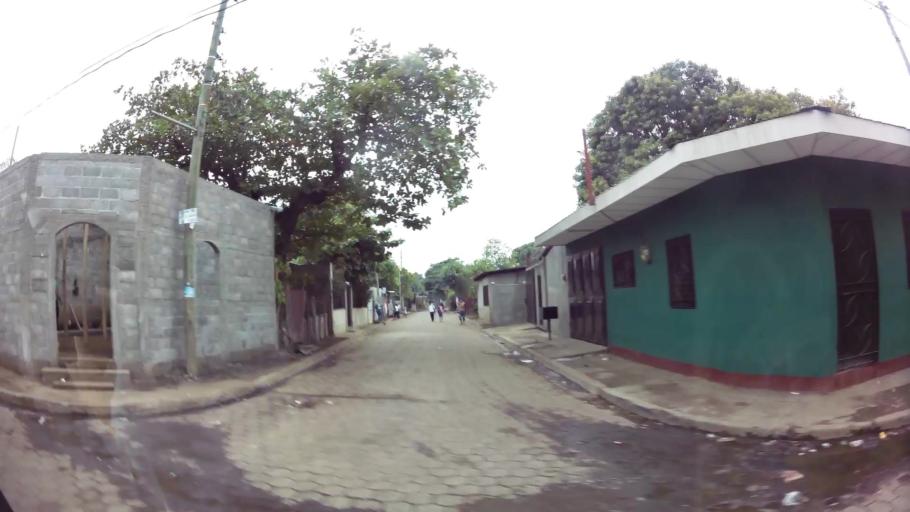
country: NI
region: Chinandega
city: Chinandega
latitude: 12.6172
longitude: -87.1172
